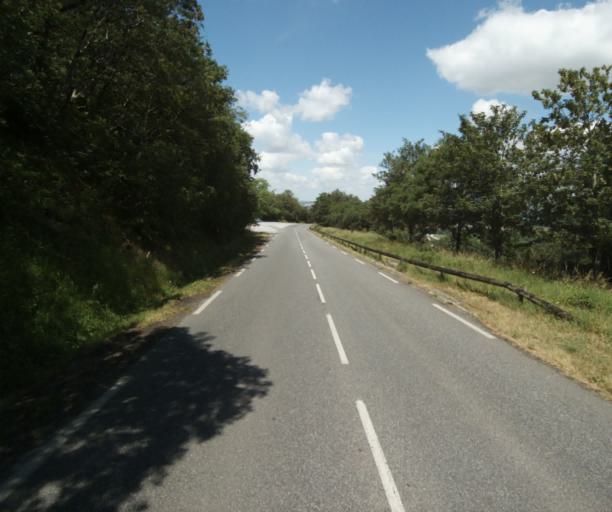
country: FR
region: Midi-Pyrenees
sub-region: Departement de la Haute-Garonne
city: Revel
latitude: 43.4437
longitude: 2.0203
